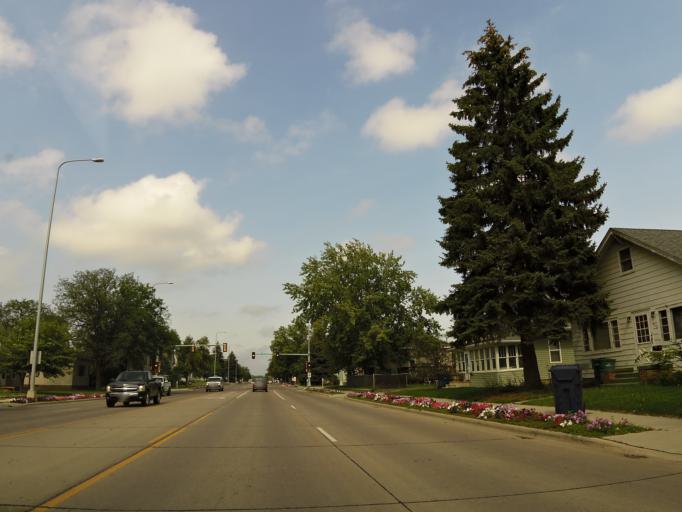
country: US
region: South Dakota
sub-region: Codington County
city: Watertown
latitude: 44.8935
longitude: -97.1085
